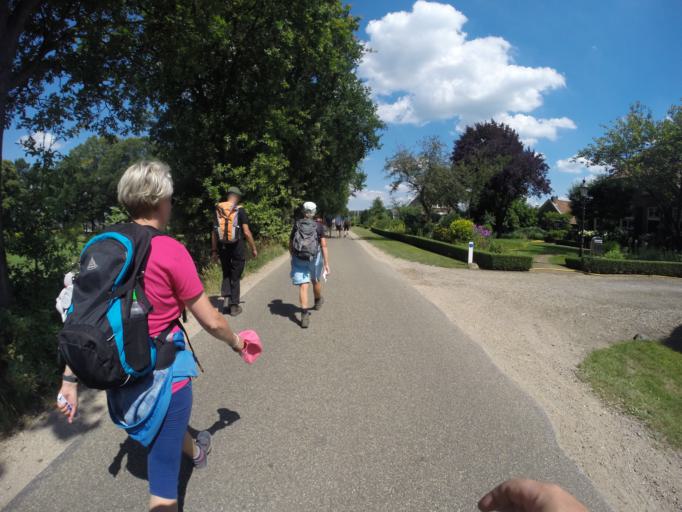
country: NL
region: Gelderland
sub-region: Gemeente Lochem
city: Barchem
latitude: 52.1186
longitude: 6.4349
